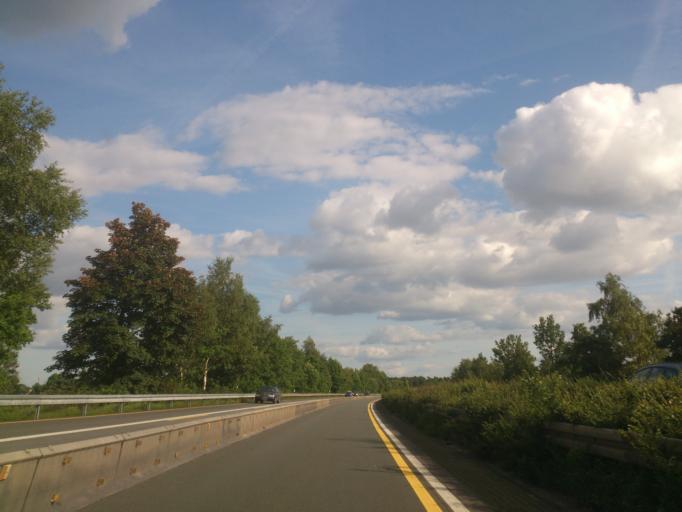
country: DE
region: North Rhine-Westphalia
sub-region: Regierungsbezirk Detmold
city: Hovelhof
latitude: 51.8269
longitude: 8.6989
